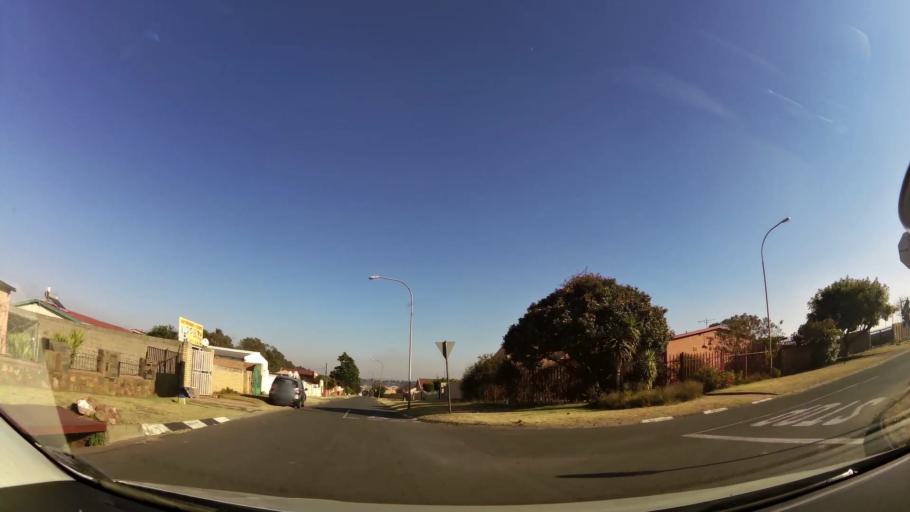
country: ZA
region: Gauteng
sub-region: City of Johannesburg Metropolitan Municipality
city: Johannesburg
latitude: -26.2080
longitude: 27.9610
